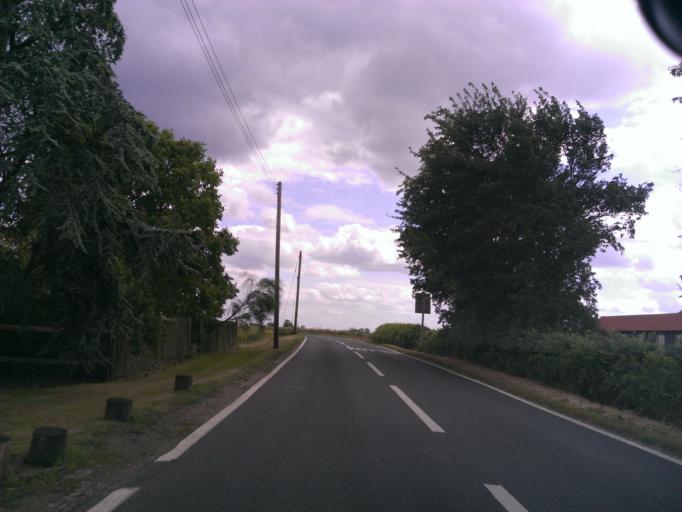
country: GB
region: England
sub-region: Essex
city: Witham
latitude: 51.8343
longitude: 0.6487
